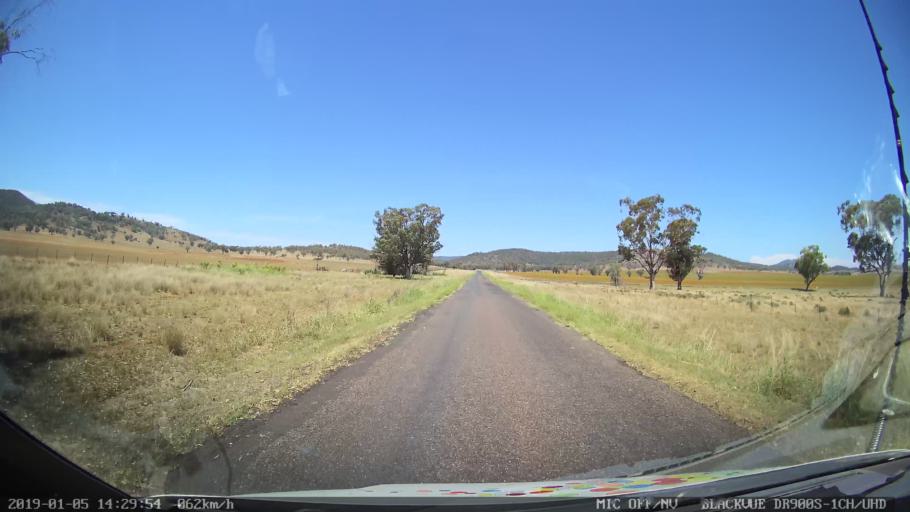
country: AU
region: New South Wales
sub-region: Tamworth Municipality
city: Phillip
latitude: -31.2281
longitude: 150.5860
